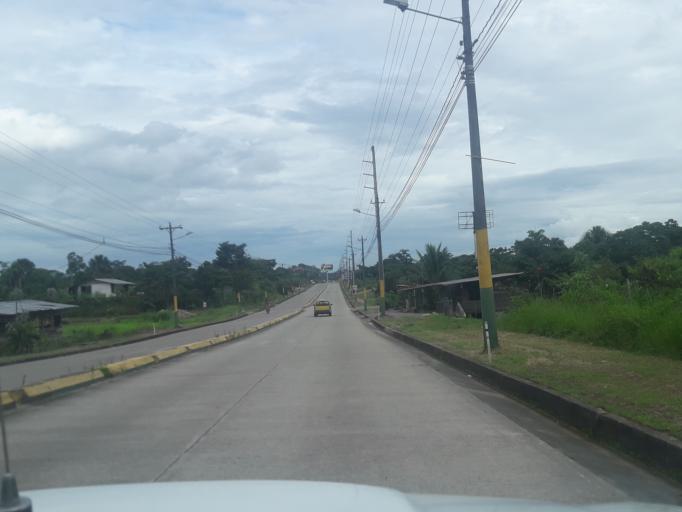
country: EC
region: Napo
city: Archidona
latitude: -0.9511
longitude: -77.8168
